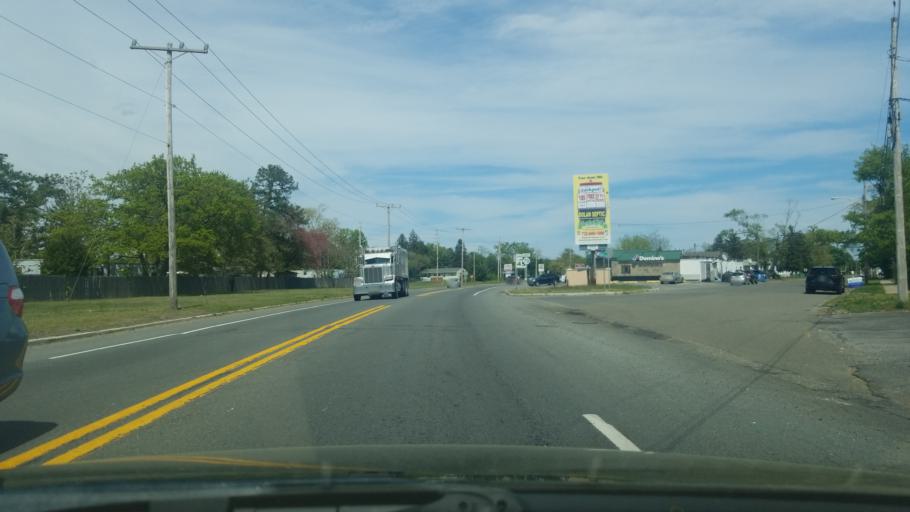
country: US
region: New Jersey
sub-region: Ocean County
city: Lakehurst
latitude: 40.0133
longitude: -74.3238
